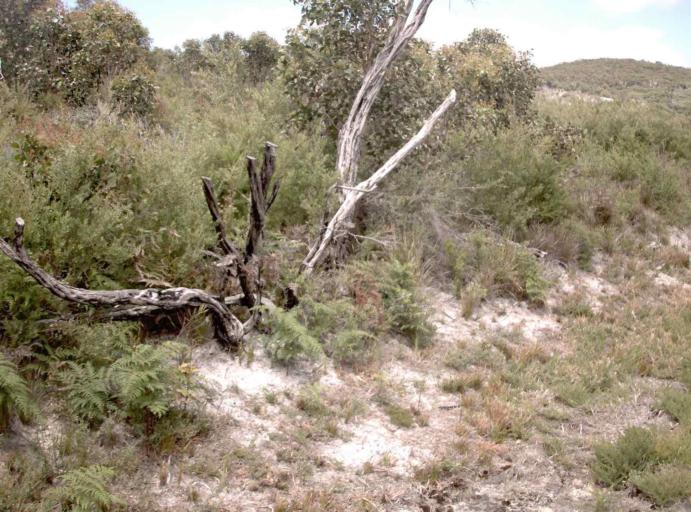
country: AU
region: Victoria
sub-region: Latrobe
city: Morwell
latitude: -39.0187
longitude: 146.3114
